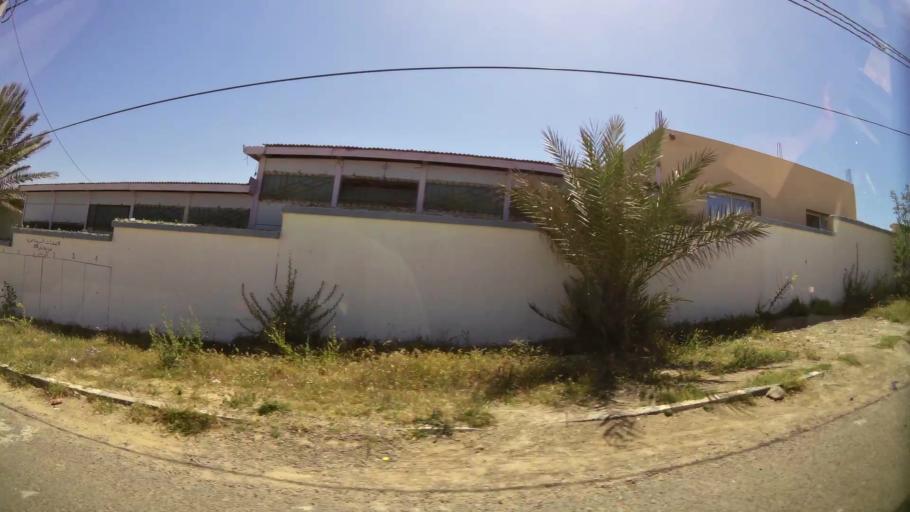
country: MA
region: Oriental
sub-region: Berkane-Taourirt
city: Madagh
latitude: 35.1406
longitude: -2.4250
